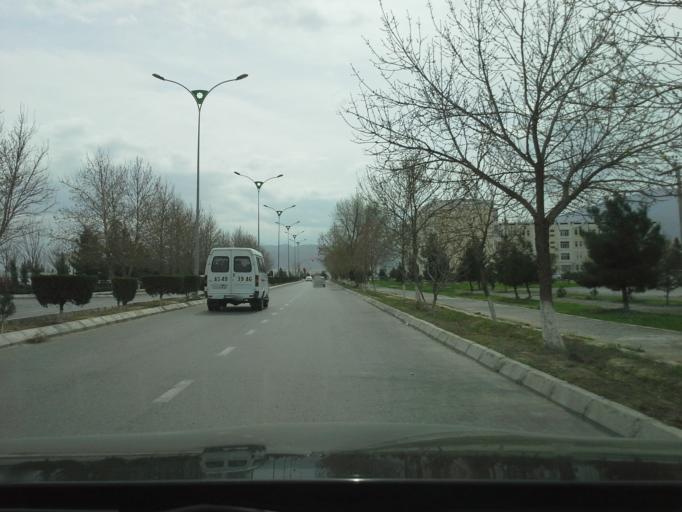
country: TM
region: Ahal
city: Abadan
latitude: 38.0557
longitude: 58.1575
